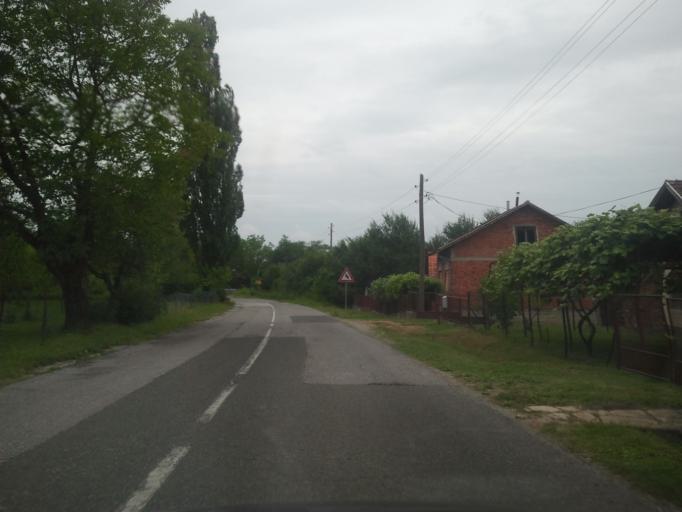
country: HR
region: Sisacko-Moslavacka
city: Gvozd
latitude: 45.4350
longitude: 15.9386
